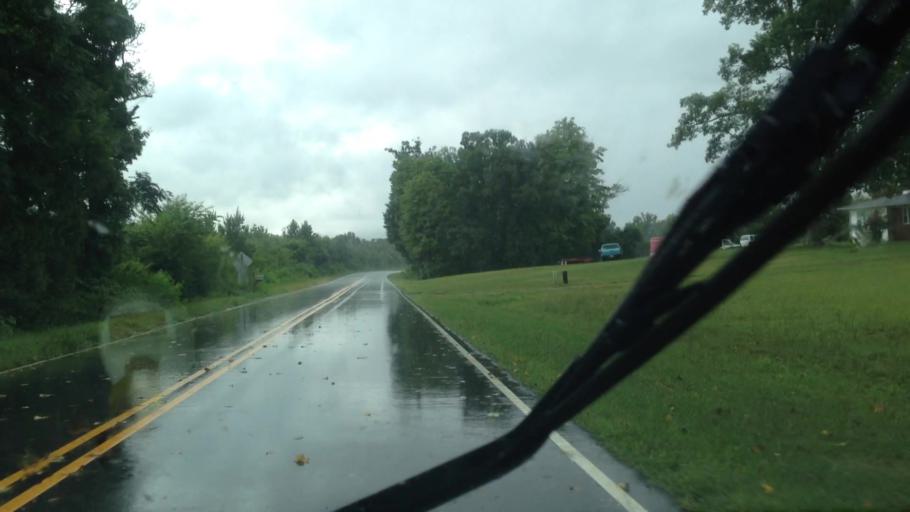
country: US
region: North Carolina
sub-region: Stokes County
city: Danbury
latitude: 36.4283
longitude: -80.0911
